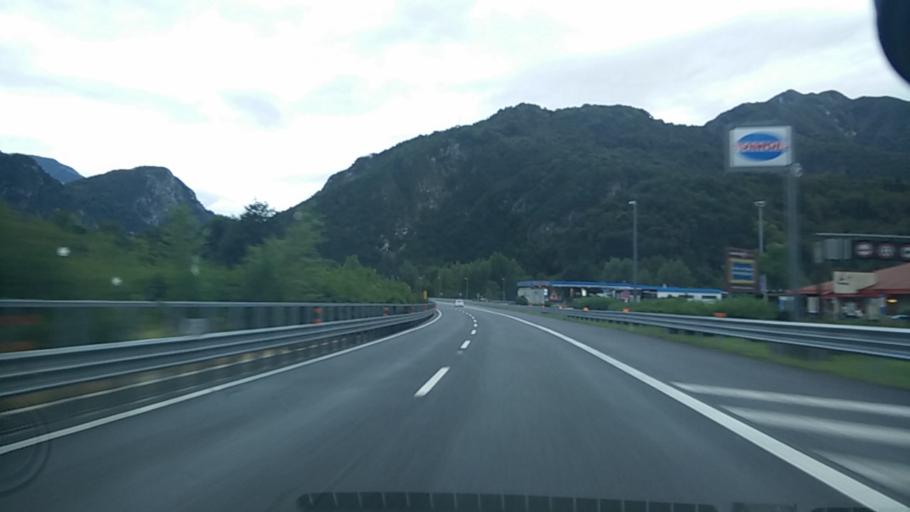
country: IT
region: Friuli Venezia Giulia
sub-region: Provincia di Udine
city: Moggio di Sotto
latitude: 46.3986
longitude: 13.1697
